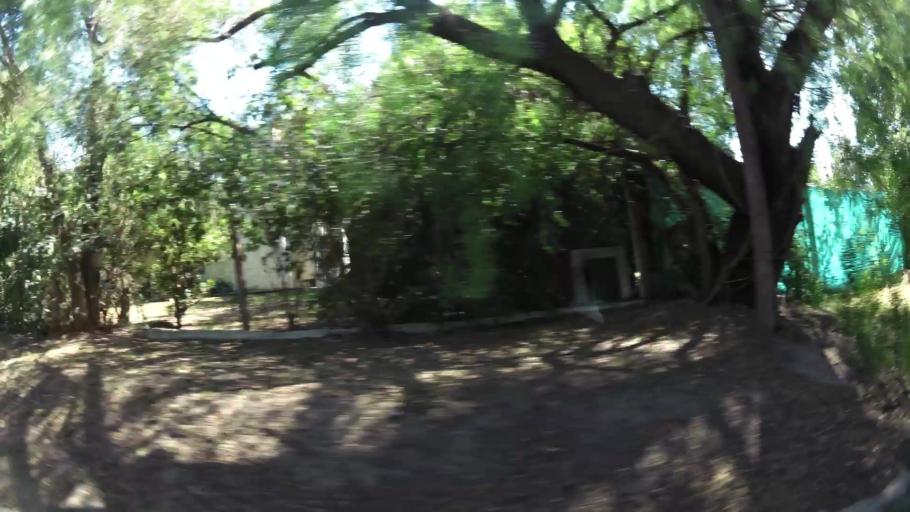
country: AR
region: Cordoba
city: Villa Allende
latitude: -31.2910
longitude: -64.2839
